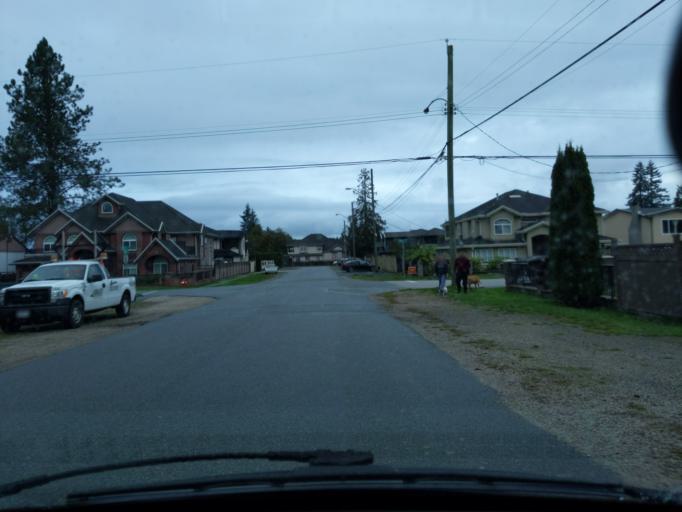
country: CA
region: British Columbia
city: New Westminster
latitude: 49.1977
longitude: -122.8624
